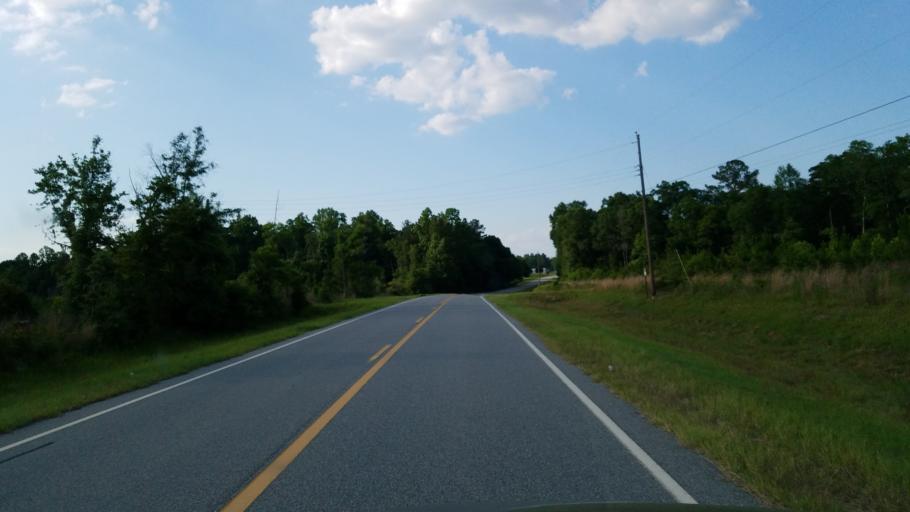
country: US
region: Georgia
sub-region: Echols County
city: Statenville
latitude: 30.7840
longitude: -83.0552
